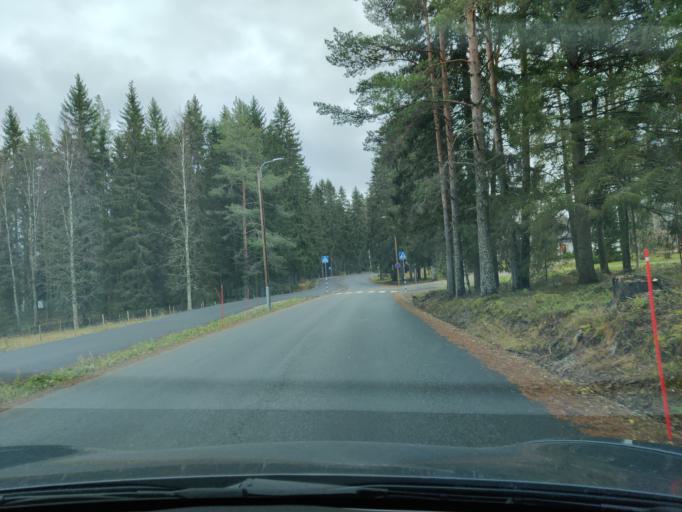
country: FI
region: Northern Savo
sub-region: Ylae-Savo
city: Kiuruvesi
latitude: 63.6473
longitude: 26.6389
